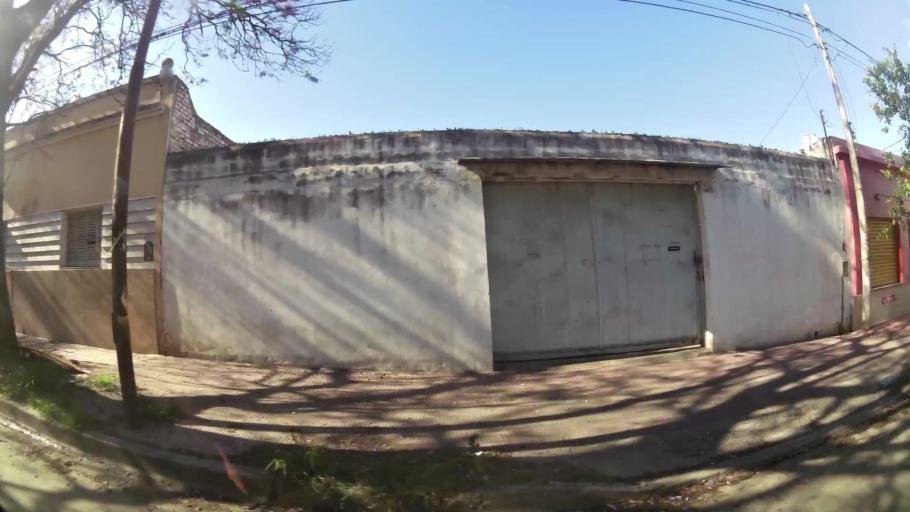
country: AR
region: Cordoba
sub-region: Departamento de Capital
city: Cordoba
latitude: -31.4262
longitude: -64.1419
